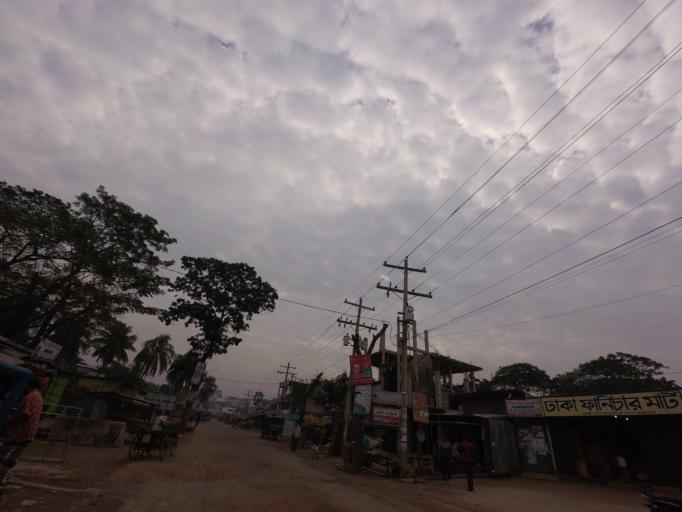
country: BD
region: Barisal
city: Nalchiti
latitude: 22.4648
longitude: 90.3783
